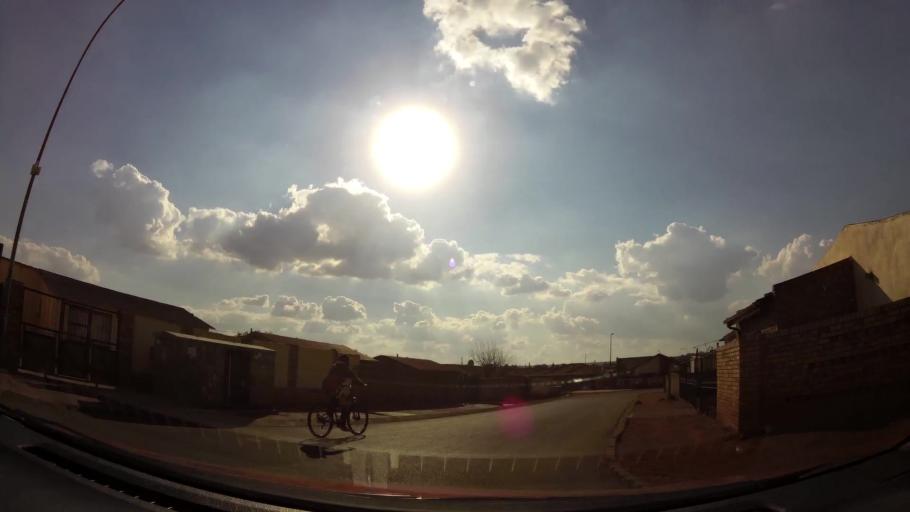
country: ZA
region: Gauteng
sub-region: City of Johannesburg Metropolitan Municipality
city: Soweto
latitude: -26.2242
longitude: 27.8702
